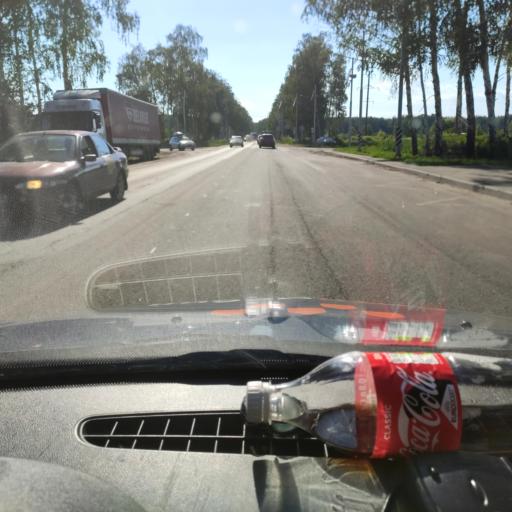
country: RU
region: Voronezj
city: Podgornoye
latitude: 51.7851
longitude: 39.1892
